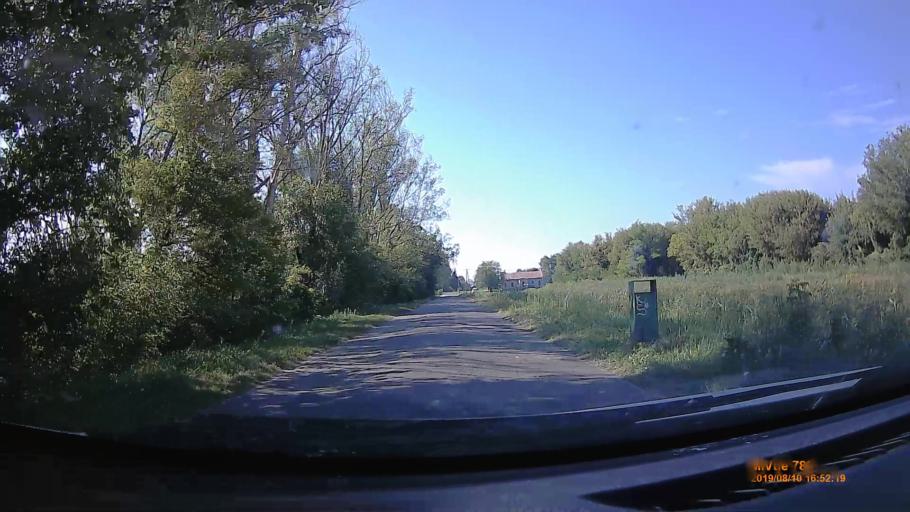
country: HU
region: Somogy
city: Balatonfenyves
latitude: 46.7056
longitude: 17.4819
